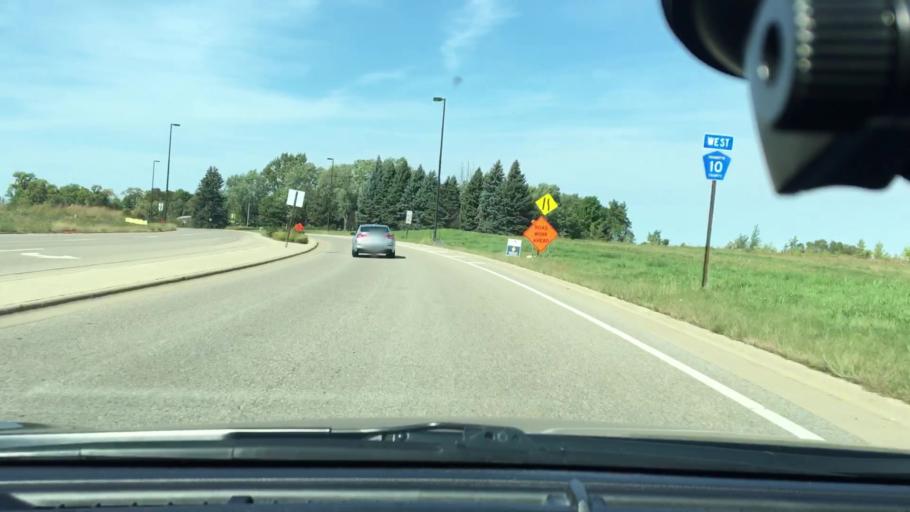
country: US
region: Minnesota
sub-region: Hennepin County
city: Corcoran
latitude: 45.0864
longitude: -93.5180
